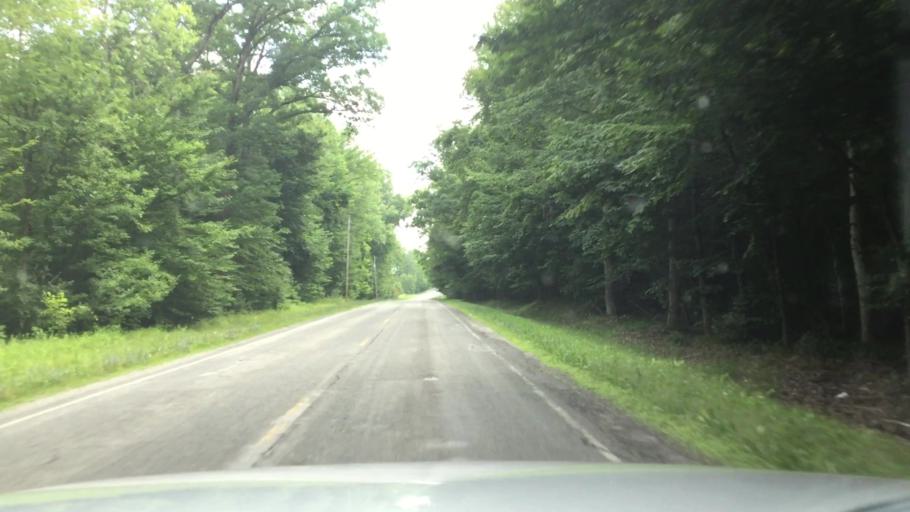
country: US
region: Michigan
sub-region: Saginaw County
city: Birch Run
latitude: 43.2942
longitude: -83.8285
